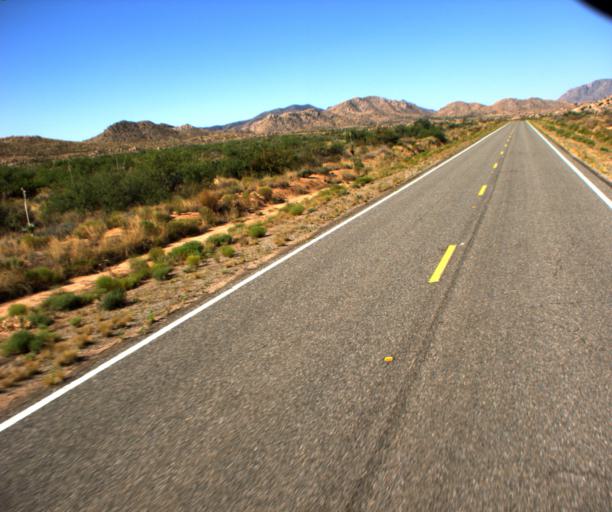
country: US
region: Arizona
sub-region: Graham County
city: Swift Trail Junction
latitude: 32.5808
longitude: -109.7076
